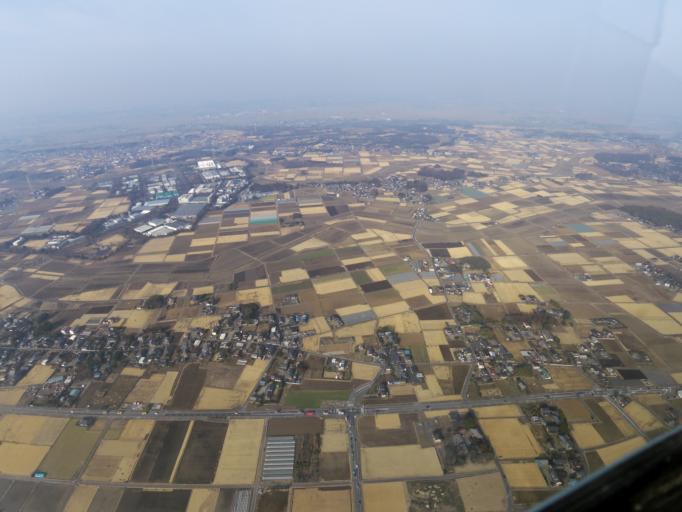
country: JP
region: Ibaraki
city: Ishige
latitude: 36.1199
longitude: 140.0431
